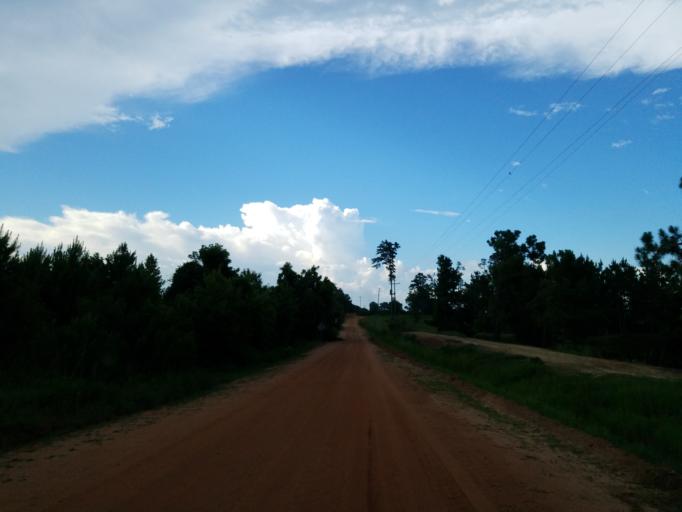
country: US
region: Georgia
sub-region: Tift County
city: Omega
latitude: 31.2734
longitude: -83.5277
